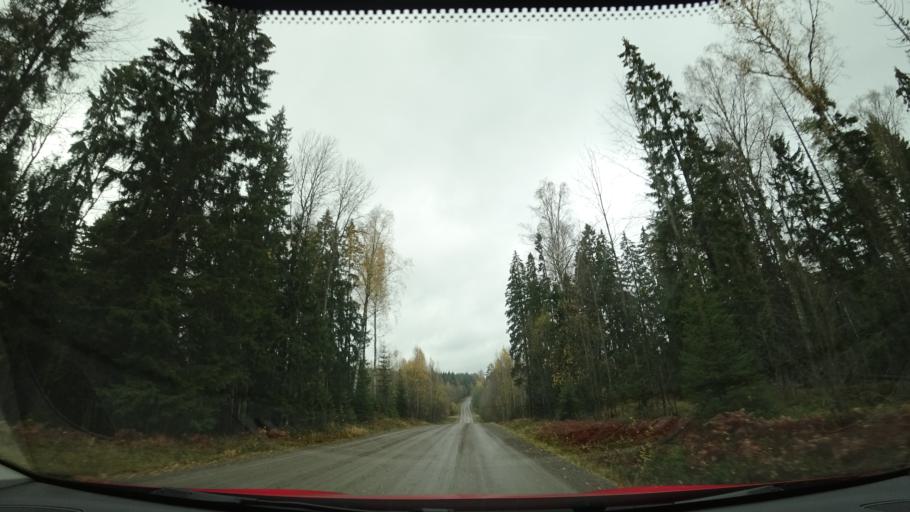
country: FI
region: Uusimaa
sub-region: Helsinki
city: Sibbo
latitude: 60.3010
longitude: 25.1987
